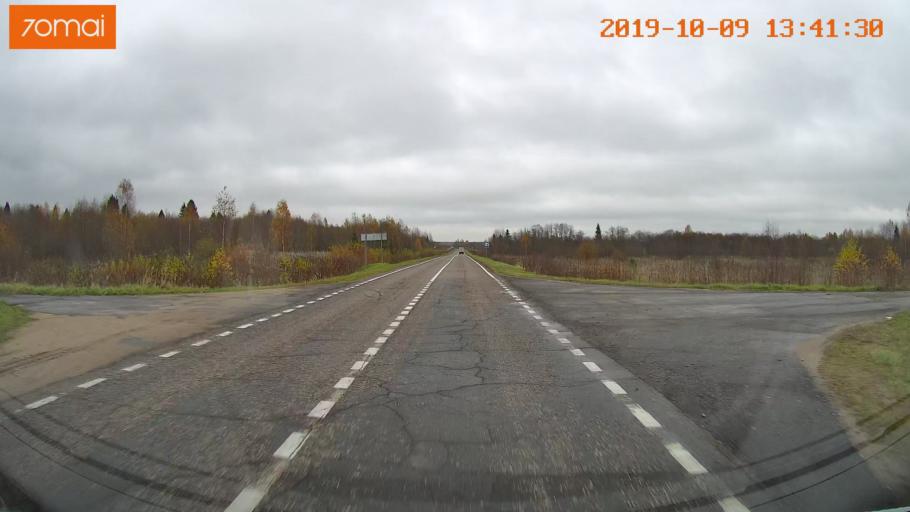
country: RU
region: Kostroma
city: Buy
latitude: 58.3515
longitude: 41.1705
